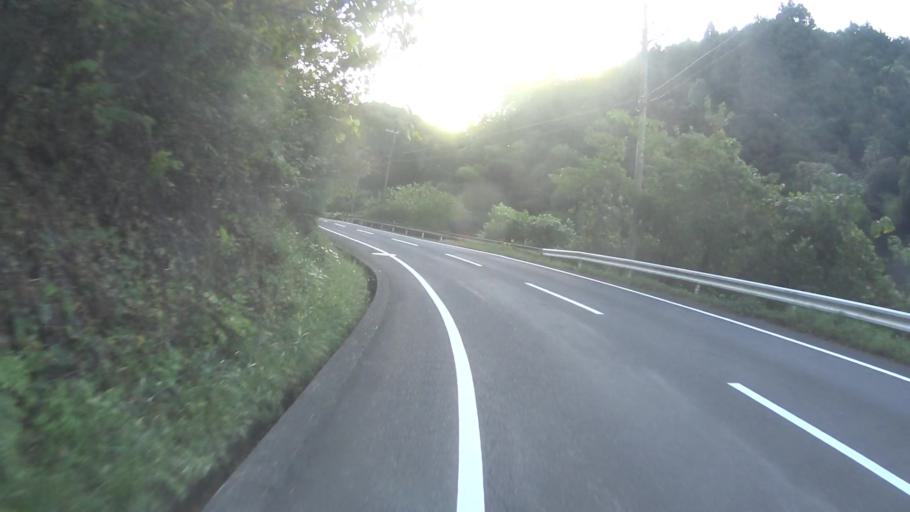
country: JP
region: Kyoto
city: Maizuru
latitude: 35.4621
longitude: 135.2577
